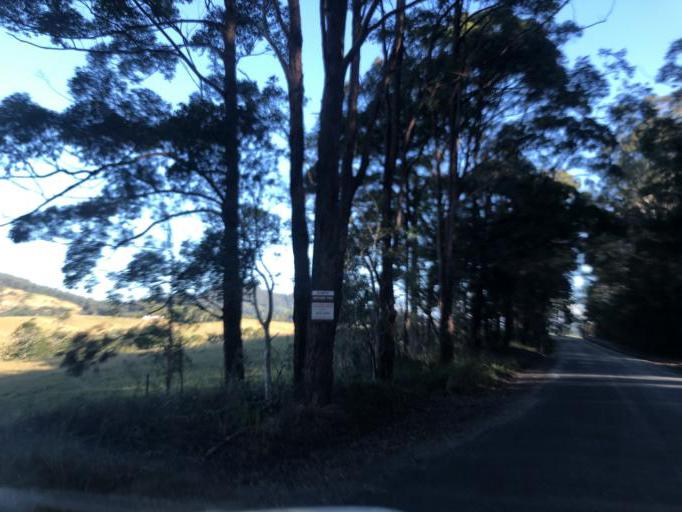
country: AU
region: New South Wales
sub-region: Nambucca Shire
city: Nambucca
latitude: -30.5824
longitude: 152.9394
